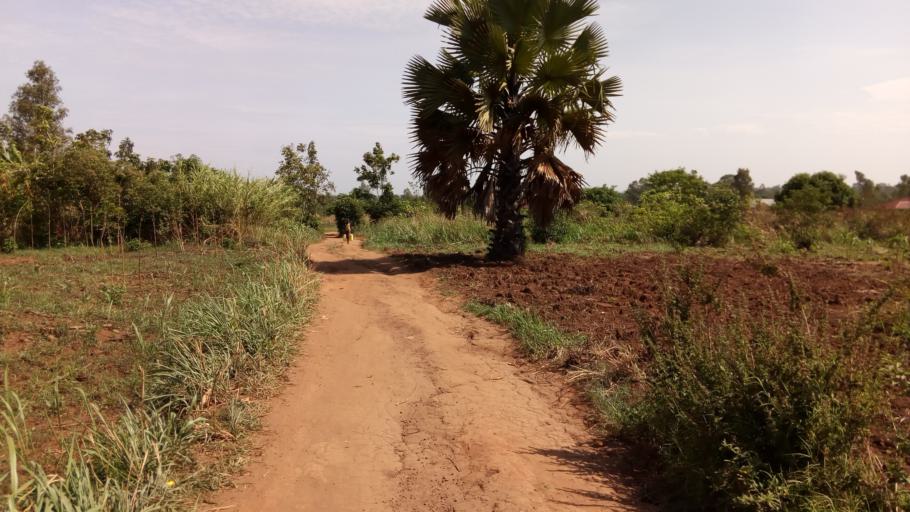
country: UG
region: Northern Region
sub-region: Gulu District
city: Gulu
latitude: 2.7932
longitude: 32.3194
